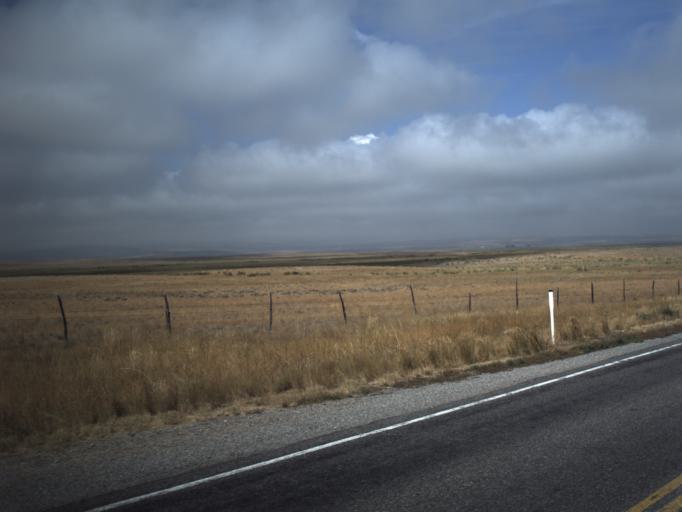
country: US
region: Utah
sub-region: Rich County
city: Randolph
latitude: 41.4607
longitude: -111.0989
